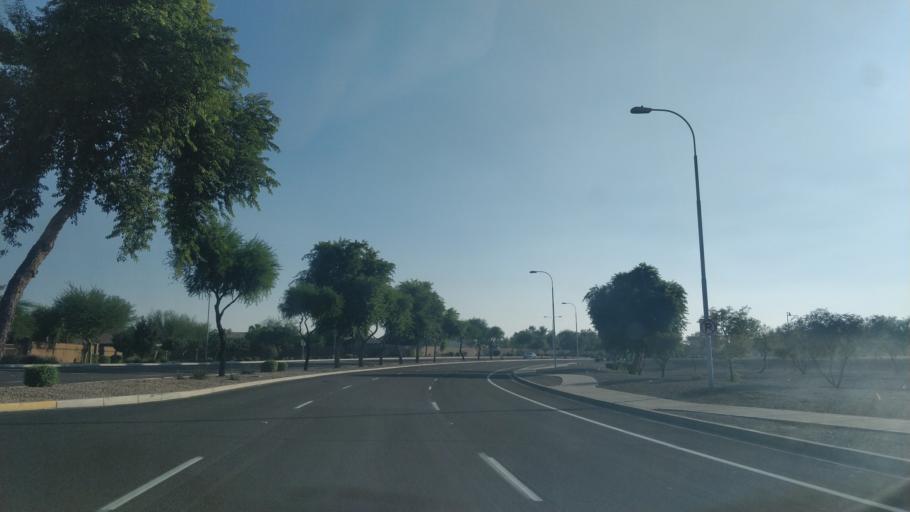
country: US
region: Arizona
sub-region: Maricopa County
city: Chandler
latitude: 33.2721
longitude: -111.8763
